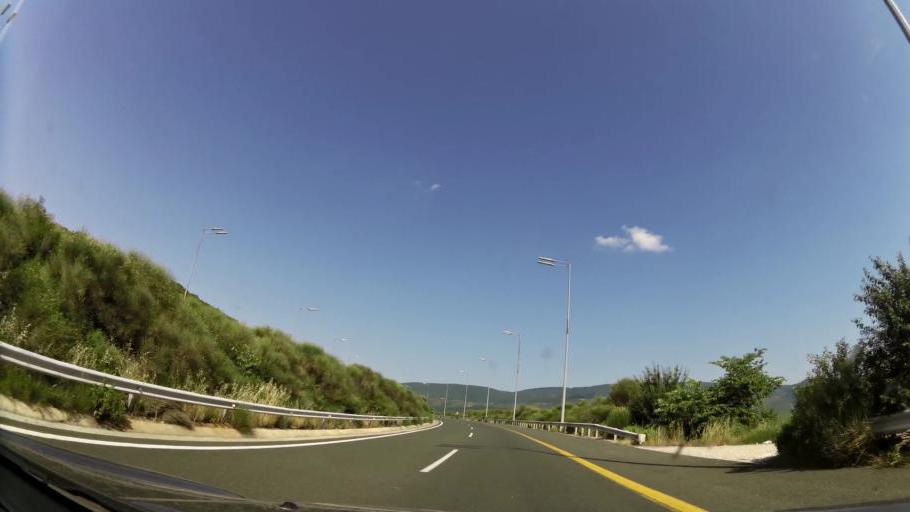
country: GR
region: Central Macedonia
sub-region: Nomos Imathias
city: Veroia
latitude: 40.4404
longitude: 22.1919
